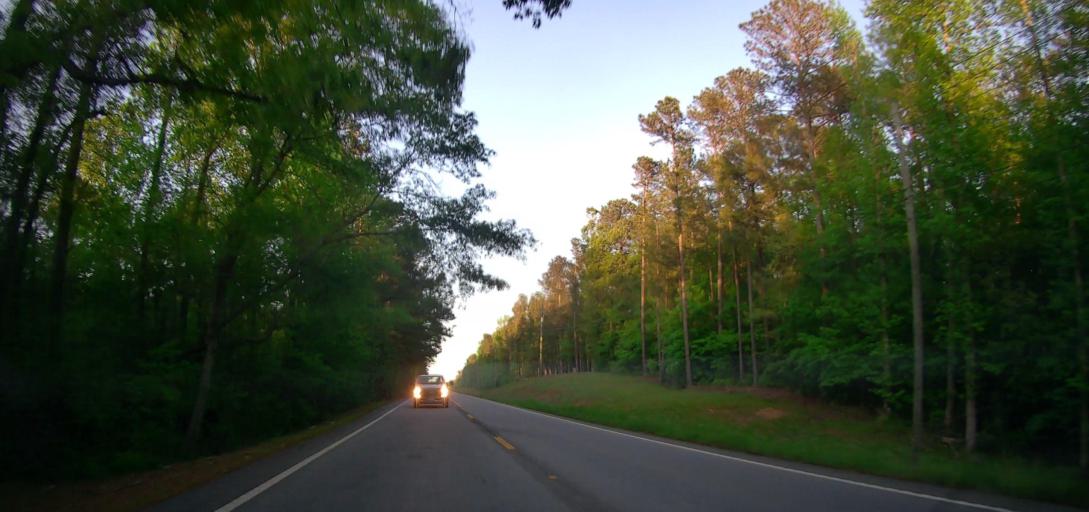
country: US
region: Georgia
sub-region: Newton County
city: Oakwood
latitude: 33.4503
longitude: -83.9842
